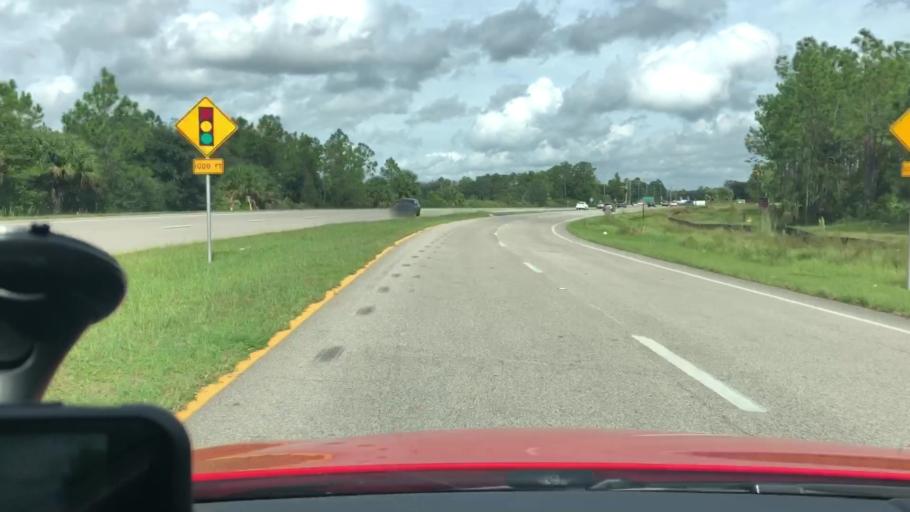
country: US
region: Florida
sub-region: Volusia County
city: Holly Hill
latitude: 29.2239
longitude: -81.0855
